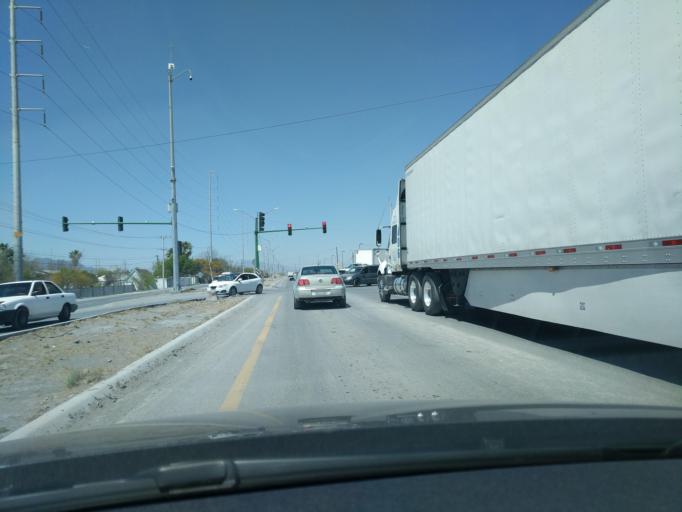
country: MX
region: Nuevo Leon
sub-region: Salinas Victoria
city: Emiliano Zapata
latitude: 25.9135
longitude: -100.2680
